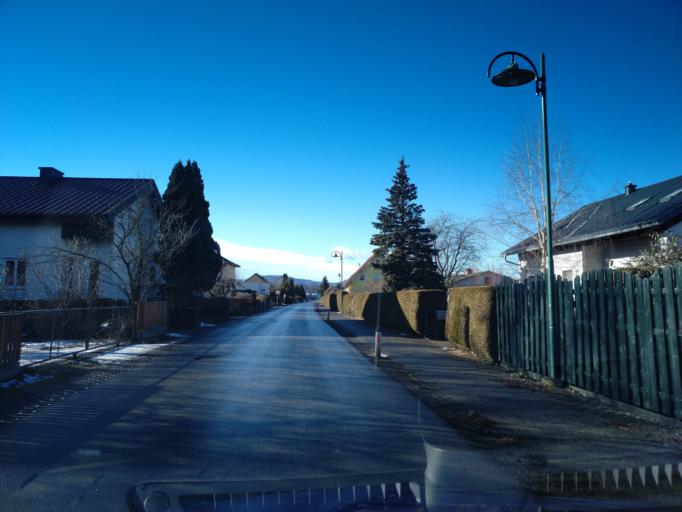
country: AT
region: Styria
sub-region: Politischer Bezirk Leibnitz
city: Kaindorf an der Sulm
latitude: 46.8177
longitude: 15.5442
